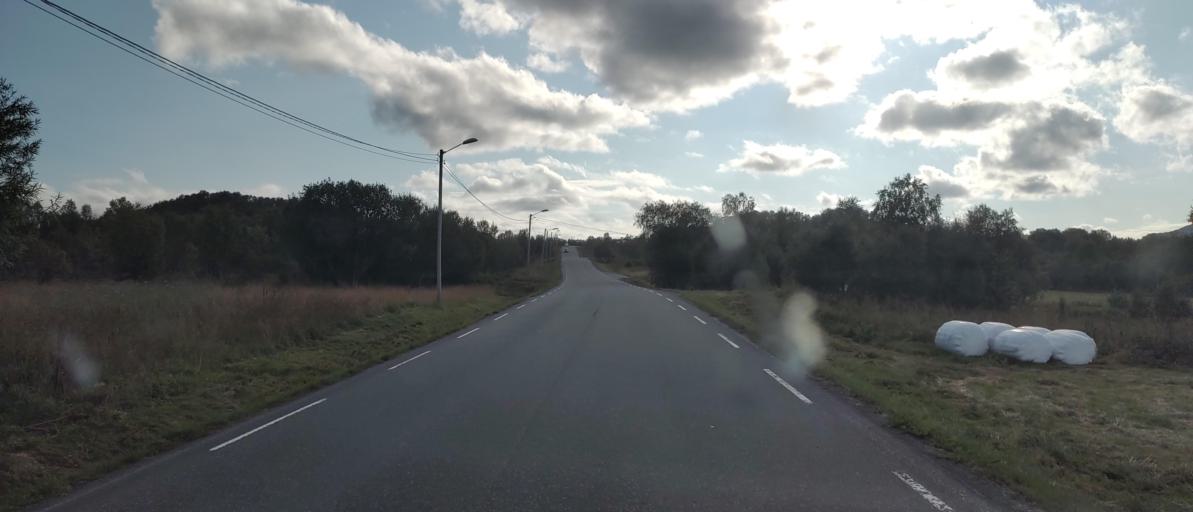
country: NO
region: Nordland
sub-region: Sortland
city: Sortland
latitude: 68.7237
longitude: 15.4718
